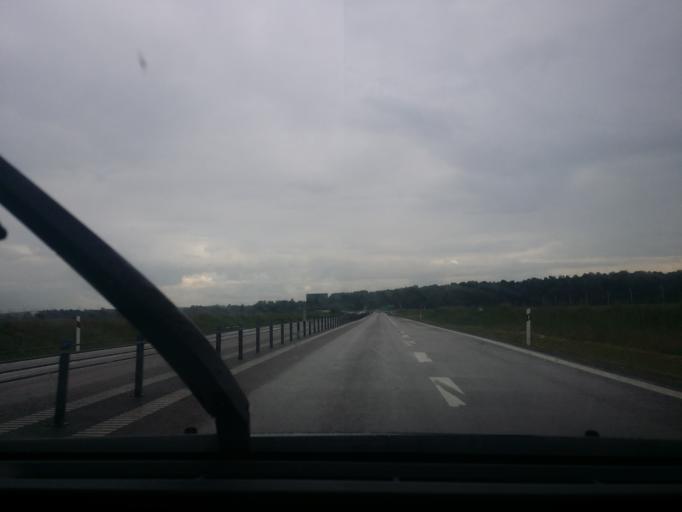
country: SE
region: Vaestmanland
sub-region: Arboga Kommun
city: Arboga
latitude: 59.4262
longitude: 15.8902
